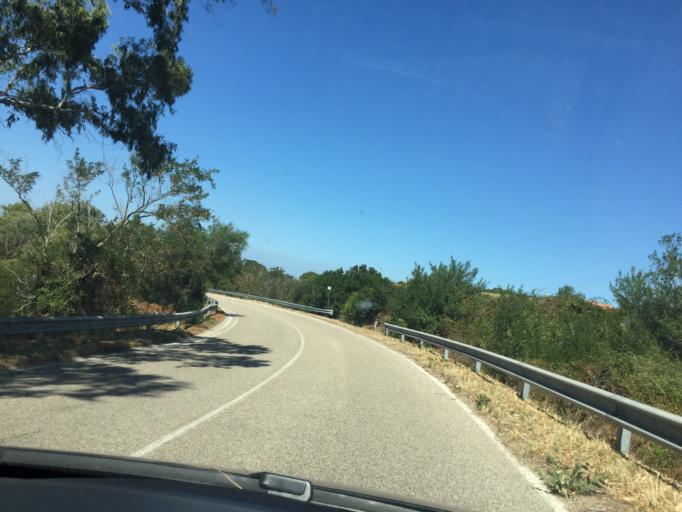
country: IT
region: Sardinia
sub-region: Provincia di Olbia-Tempio
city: Aglientu
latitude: 41.1036
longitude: 9.0863
